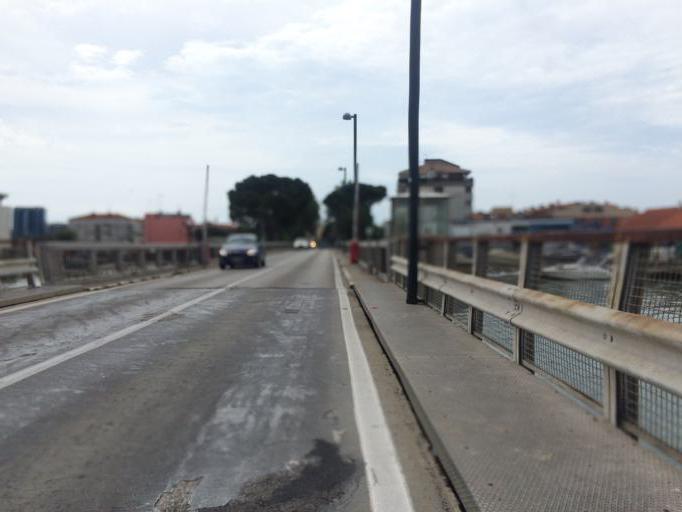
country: IT
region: Friuli Venezia Giulia
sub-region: Provincia di Gorizia
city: Grado
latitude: 45.6836
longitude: 13.3863
